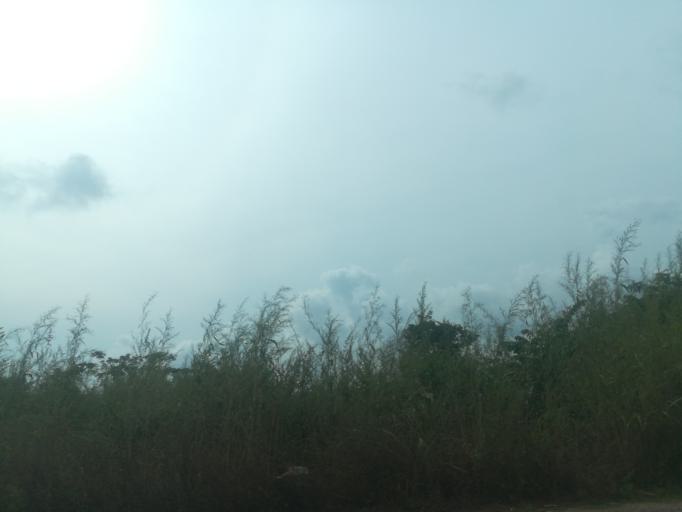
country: NG
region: Ogun
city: Ayetoro
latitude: 7.3218
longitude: 3.0683
